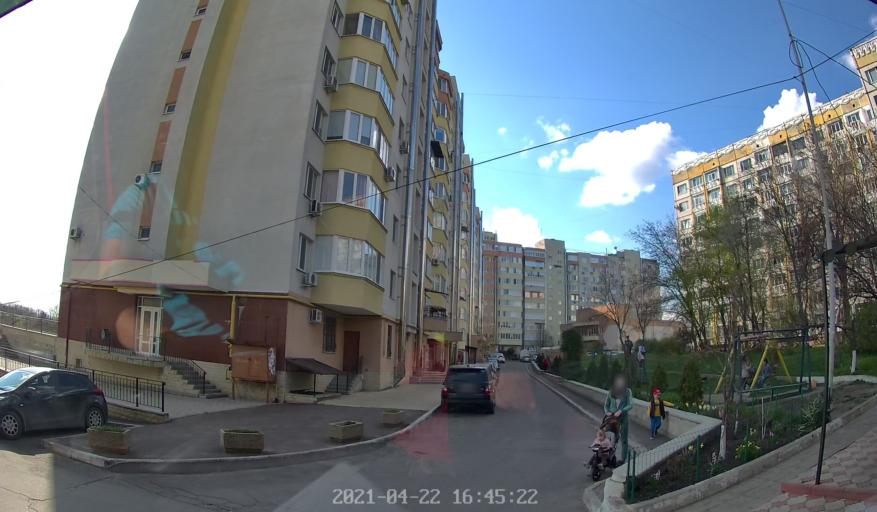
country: NG
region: Niger
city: Lemu
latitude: 9.4082
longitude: 5.7765
